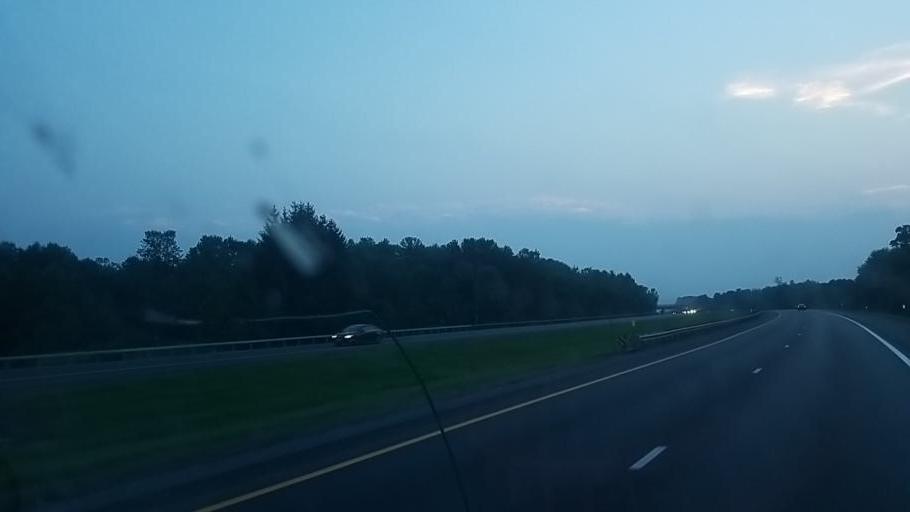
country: US
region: New York
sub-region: Oneida County
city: Rome
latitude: 43.1363
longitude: -75.4805
